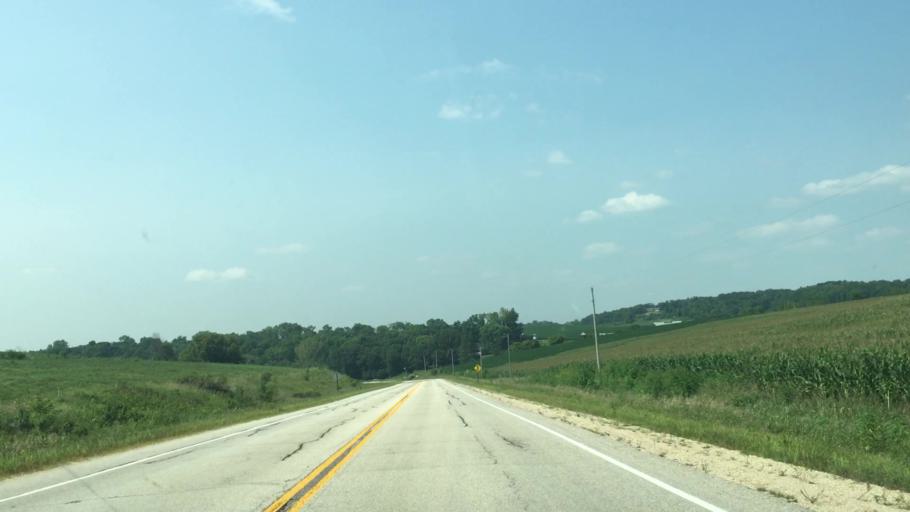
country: US
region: Minnesota
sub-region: Fillmore County
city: Preston
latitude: 43.6930
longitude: -91.9518
